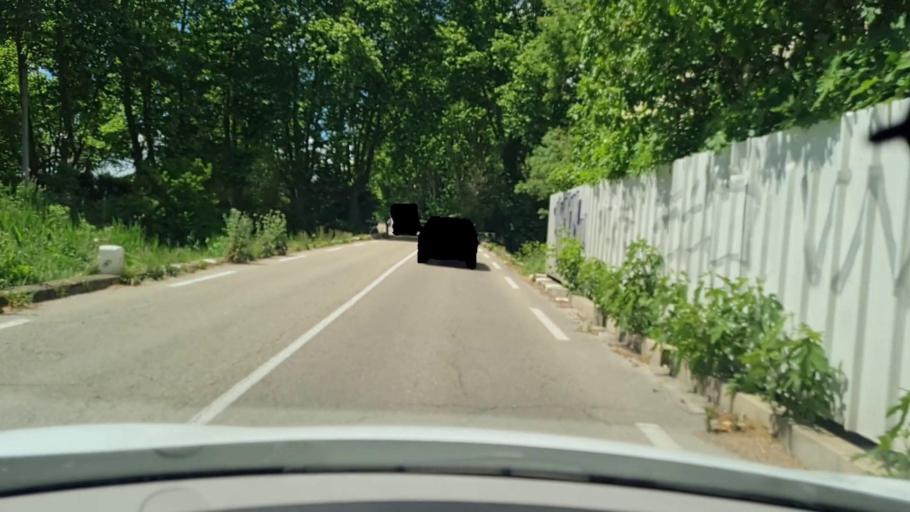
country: FR
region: Languedoc-Roussillon
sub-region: Departement du Gard
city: Le Cailar
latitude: 43.6876
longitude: 4.2466
